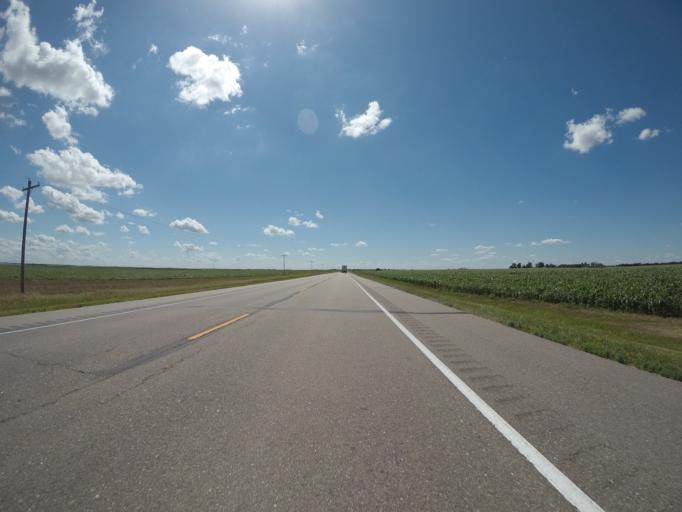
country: US
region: Nebraska
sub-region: Chase County
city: Imperial
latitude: 40.4944
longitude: -101.5837
